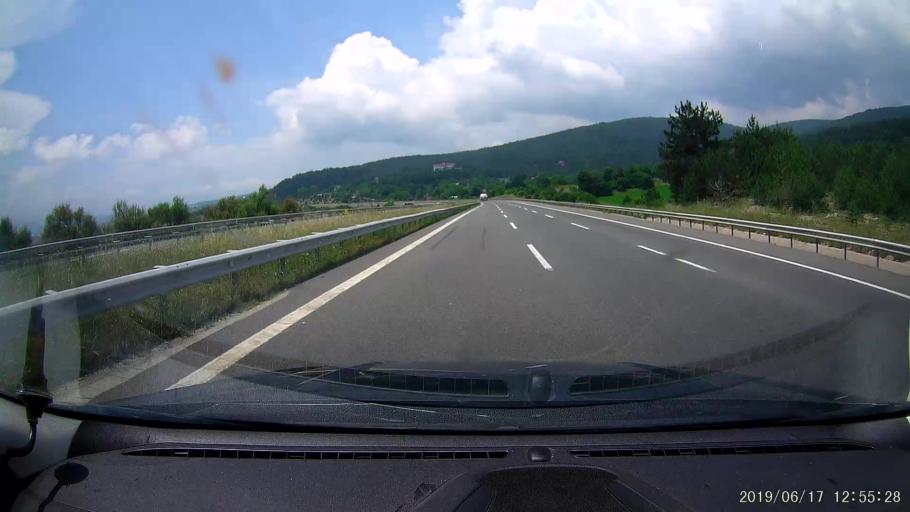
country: TR
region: Bolu
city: Bolu
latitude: 40.7610
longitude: 31.5937
